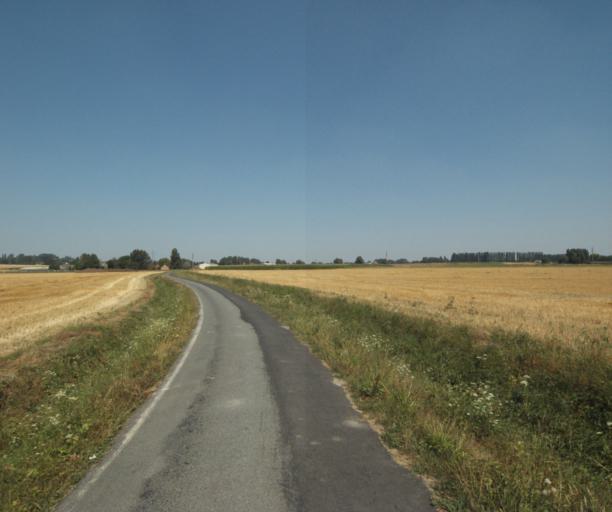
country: FR
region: Nord-Pas-de-Calais
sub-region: Departement du Nord
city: Wervicq-Sud
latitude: 50.7458
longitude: 3.0476
